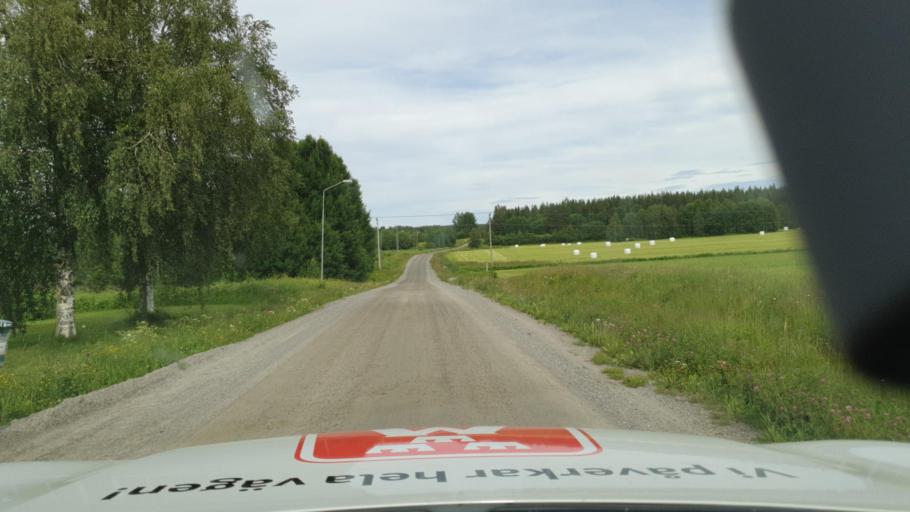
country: SE
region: Vaesterbotten
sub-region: Skelleftea Kommun
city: Viken
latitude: 64.5118
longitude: 20.9409
